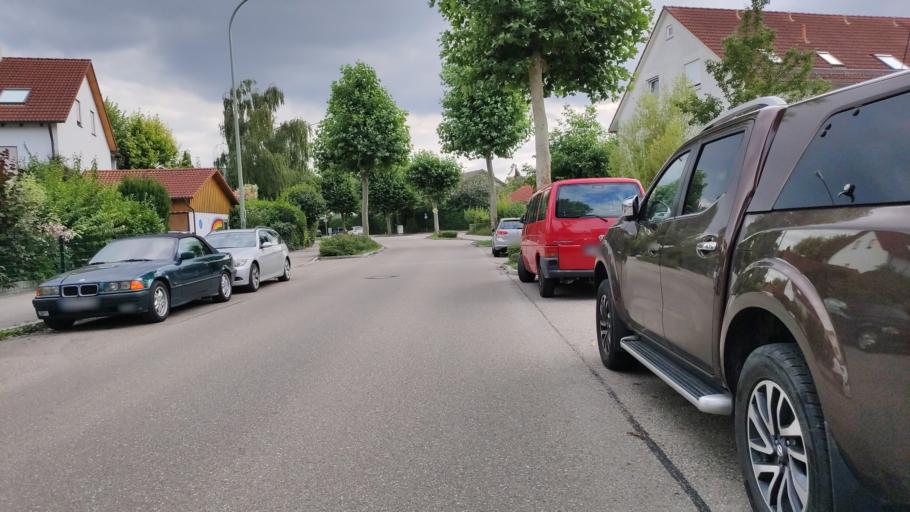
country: DE
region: Bavaria
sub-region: Swabia
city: Konigsbrunn
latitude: 48.2554
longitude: 10.8922
